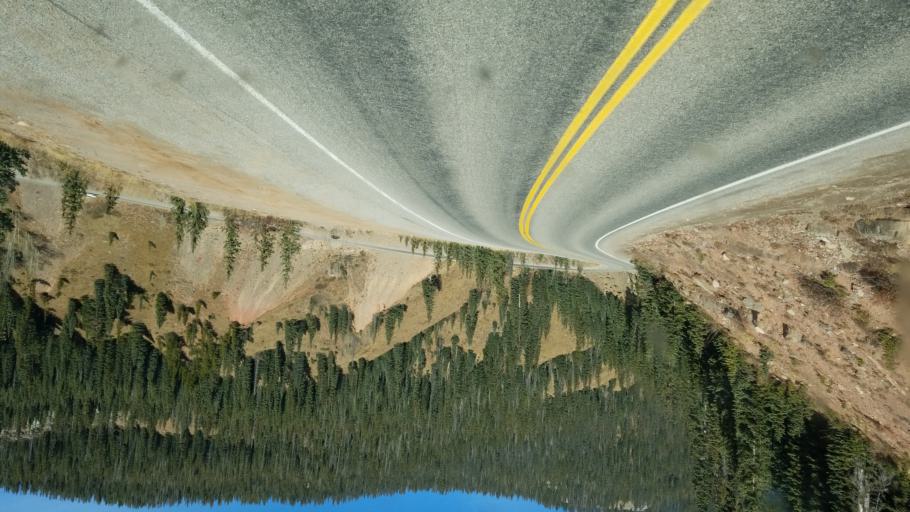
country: US
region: Colorado
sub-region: San Juan County
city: Silverton
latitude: 37.7055
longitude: -107.7691
